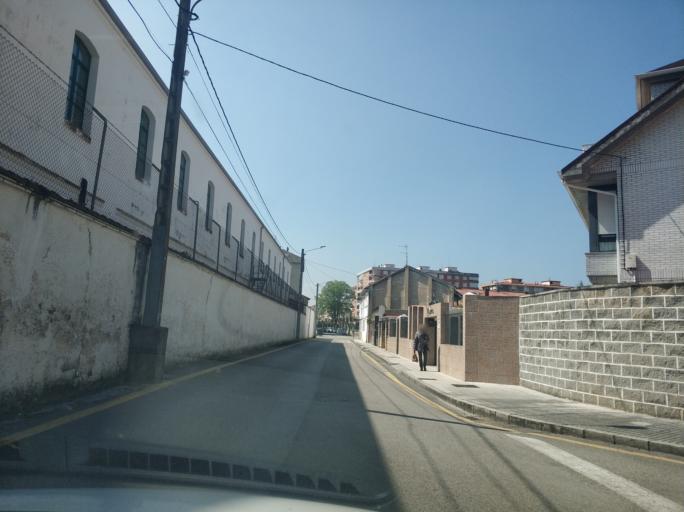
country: ES
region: Cantabria
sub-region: Provincia de Cantabria
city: Santona
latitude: 43.4406
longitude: -3.4495
